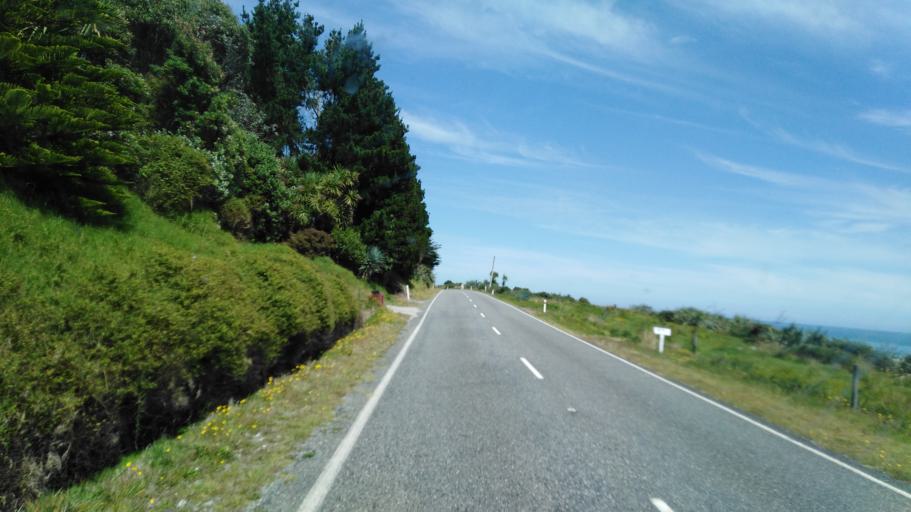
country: NZ
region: West Coast
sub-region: Buller District
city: Westport
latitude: -41.5664
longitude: 171.9106
